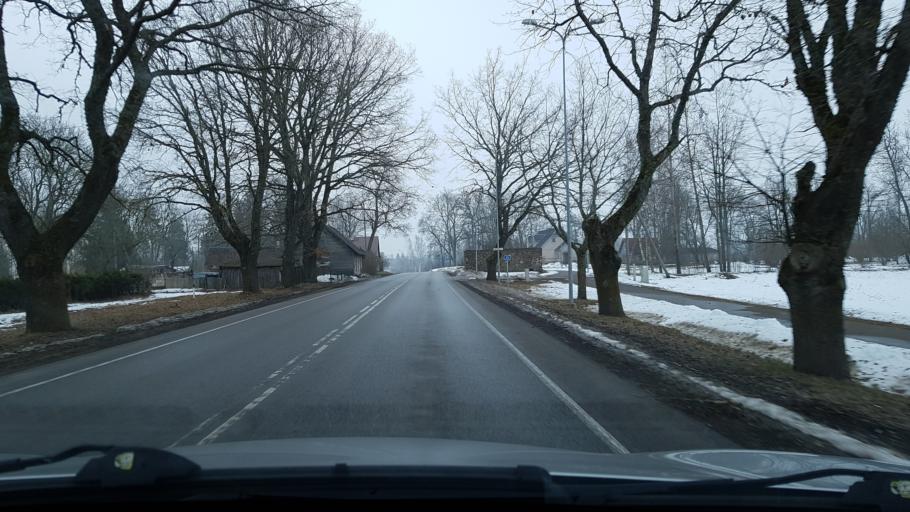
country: EE
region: Valgamaa
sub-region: Torva linn
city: Torva
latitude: 58.2317
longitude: 25.8818
